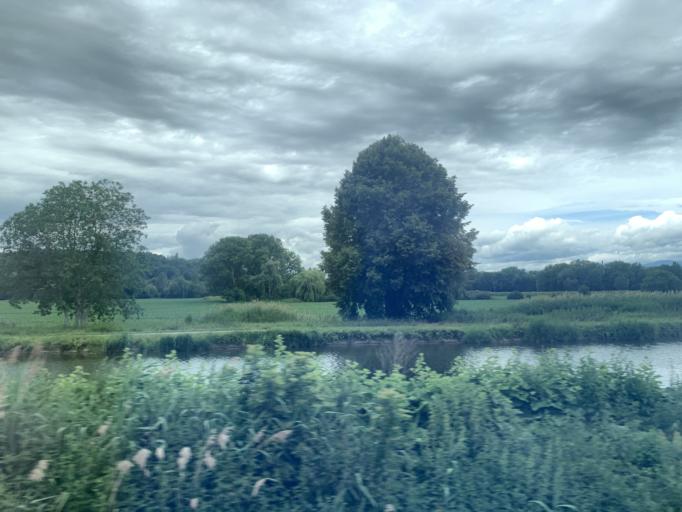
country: FR
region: Alsace
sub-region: Departement du Haut-Rhin
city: Brunstatt
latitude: 47.7163
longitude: 7.3133
